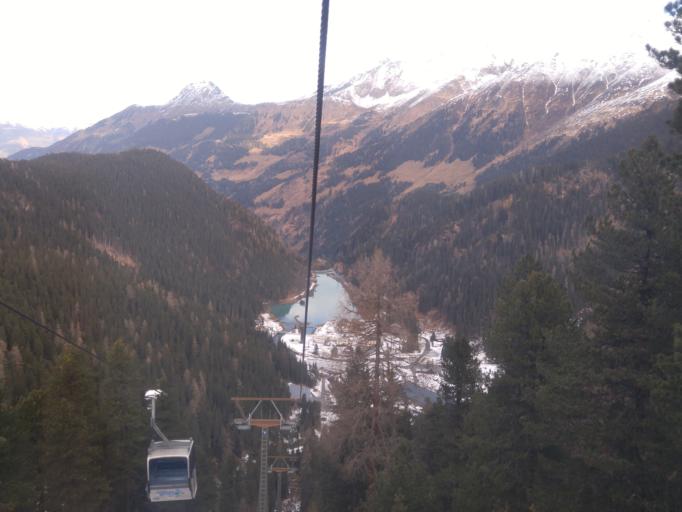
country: AT
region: Salzburg
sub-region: Politischer Bezirk Zell am See
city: Niedernsill
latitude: 47.1625
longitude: 12.6239
